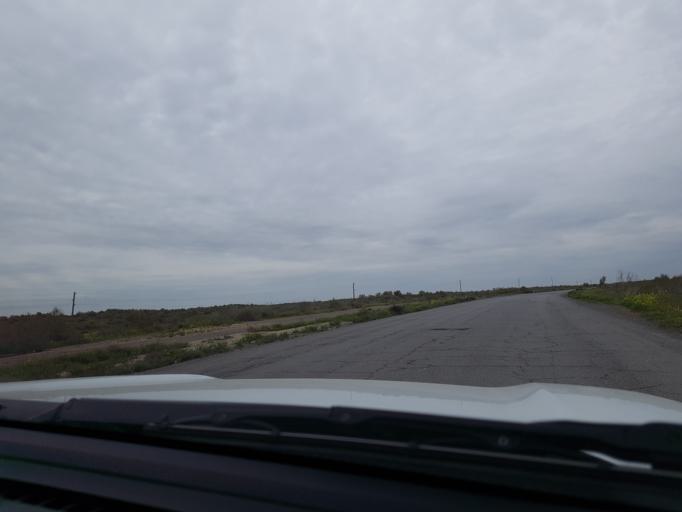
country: TM
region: Mary
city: Bayramaly
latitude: 37.8729
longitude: 62.6117
